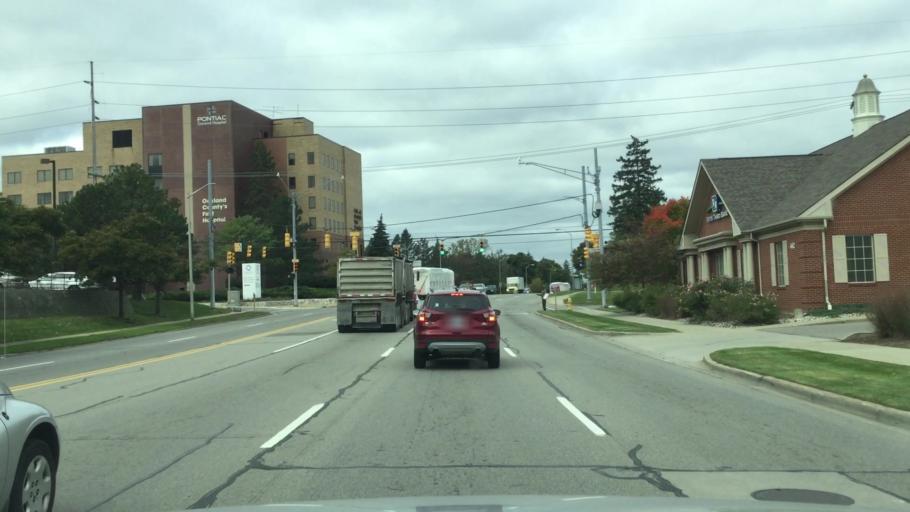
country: US
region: Michigan
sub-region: Oakland County
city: Pontiac
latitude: 42.6360
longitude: -83.3080
